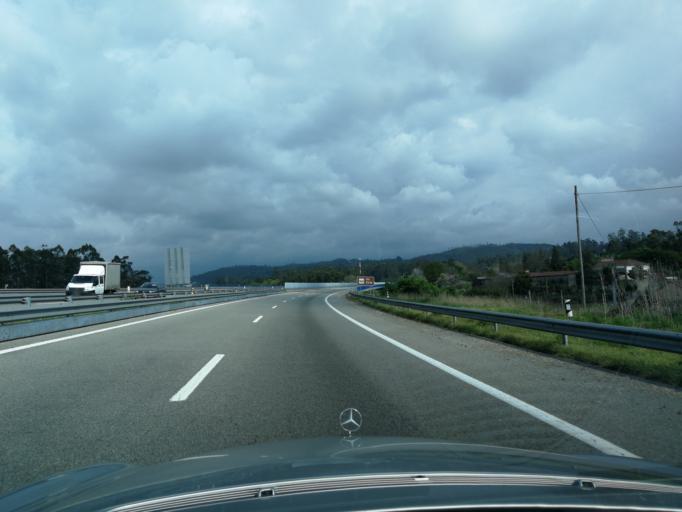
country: PT
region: Porto
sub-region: Vila do Conde
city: Arvore
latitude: 41.3936
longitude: -8.6836
